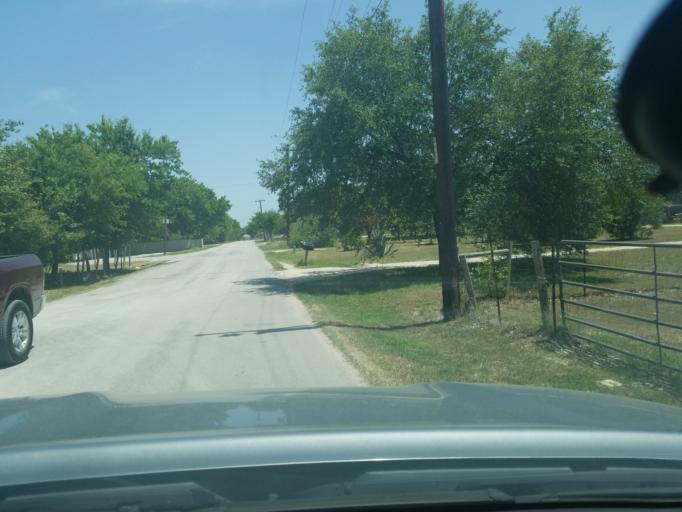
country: US
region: Texas
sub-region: Guadalupe County
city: Cibolo
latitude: 29.5777
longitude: -98.1966
